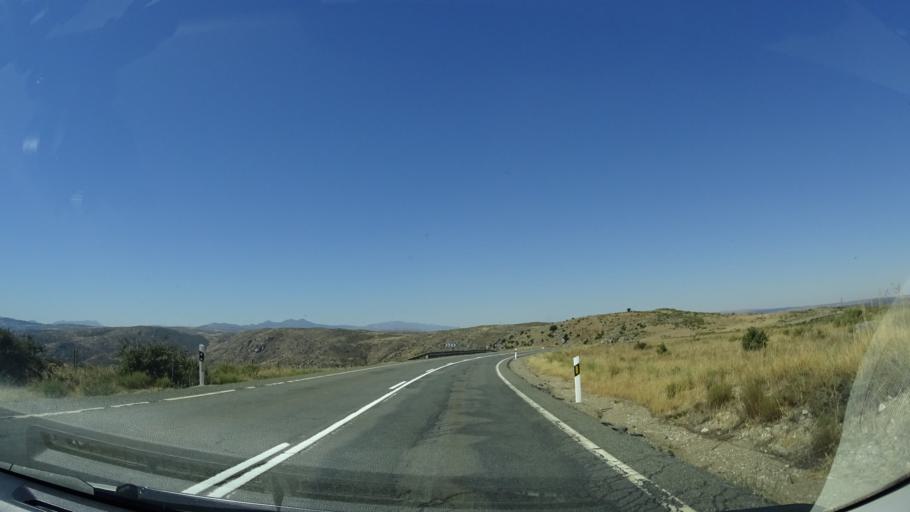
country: ES
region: Castille and Leon
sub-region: Provincia de Avila
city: Tornadizos de Avila
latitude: 40.6069
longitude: -4.5456
